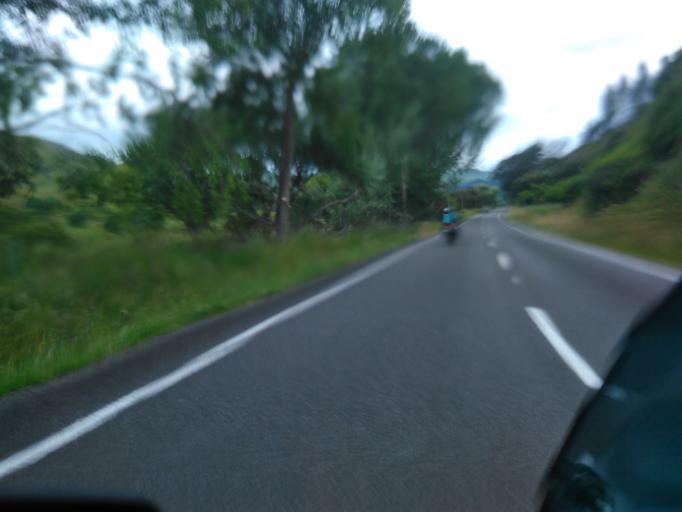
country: NZ
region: Gisborne
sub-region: Gisborne District
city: Gisborne
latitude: -38.4425
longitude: 177.6044
